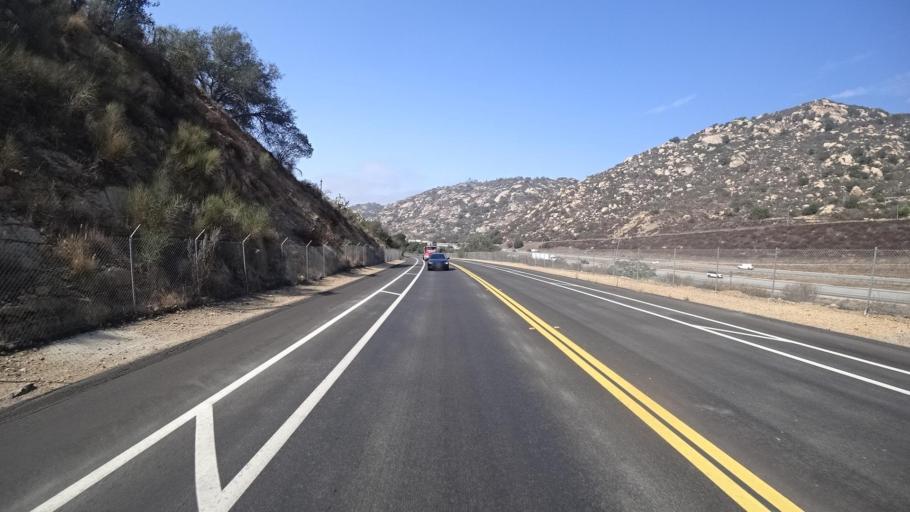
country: US
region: California
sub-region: San Diego County
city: Rainbow
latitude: 33.4281
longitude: -117.1469
